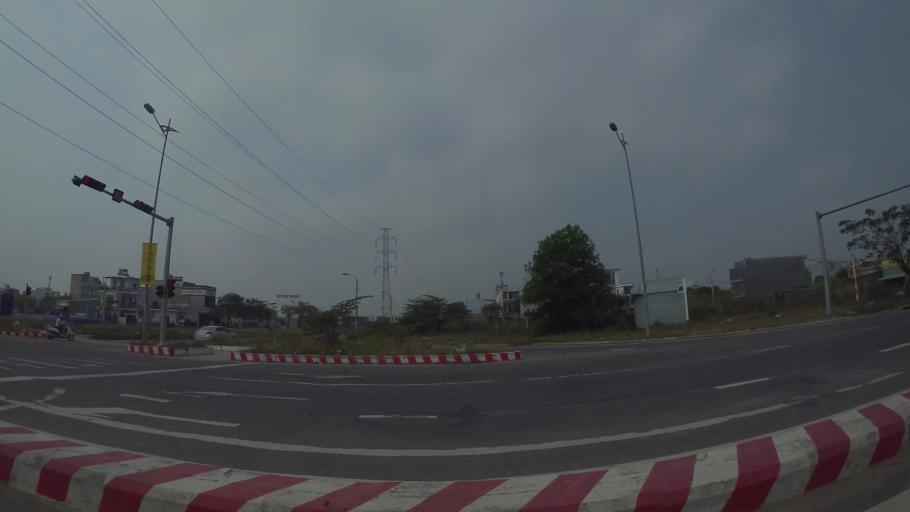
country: VN
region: Da Nang
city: Cam Le
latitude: 16.0082
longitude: 108.2193
